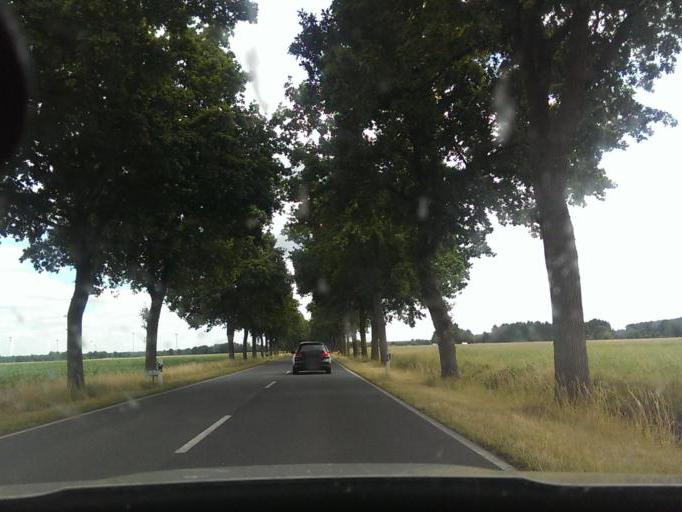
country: DE
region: Lower Saxony
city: Essel
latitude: 52.6745
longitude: 9.6549
